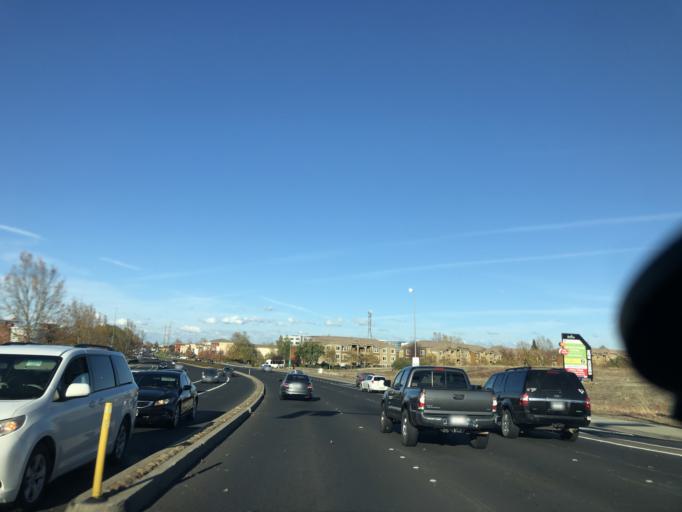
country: US
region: California
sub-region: Placer County
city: Roseville
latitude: 38.7783
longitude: -121.2879
